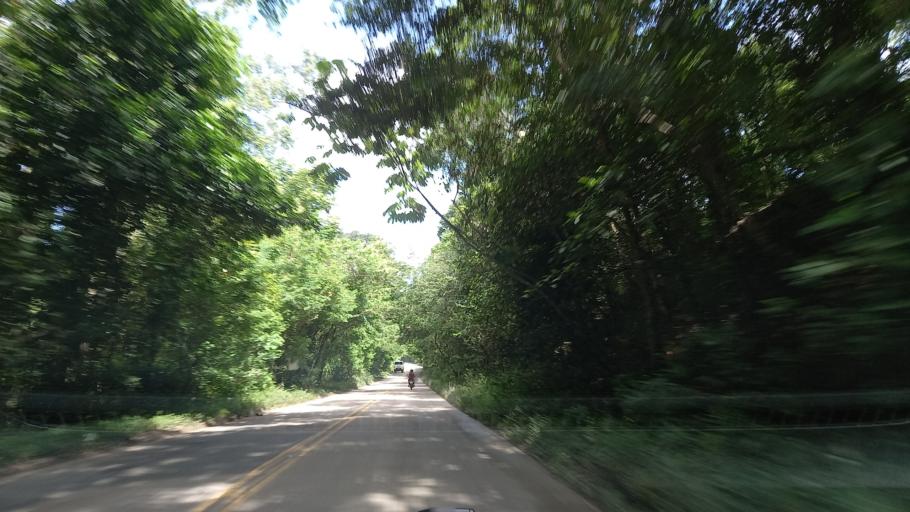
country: BR
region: Pernambuco
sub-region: Rio Formoso
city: Rio Formoso
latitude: -8.7298
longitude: -35.1733
